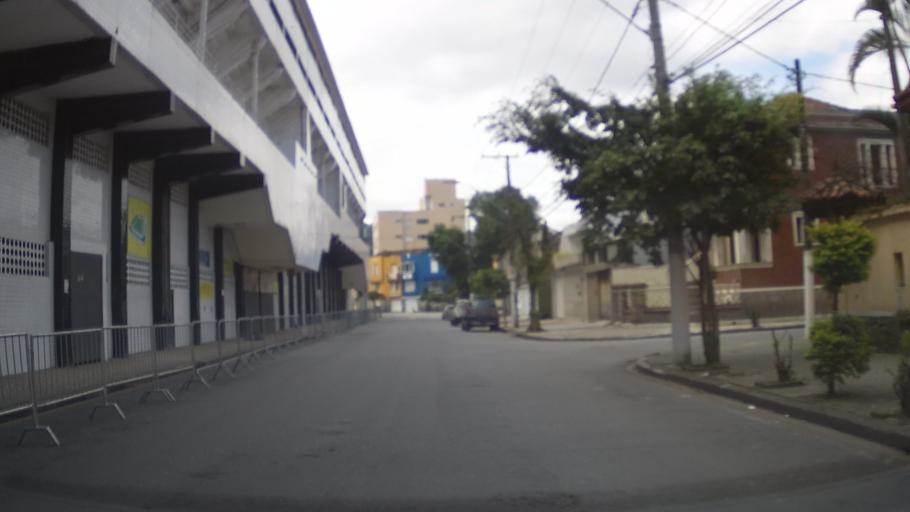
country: BR
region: Sao Paulo
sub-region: Santos
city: Santos
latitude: -23.9517
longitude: -46.3387
